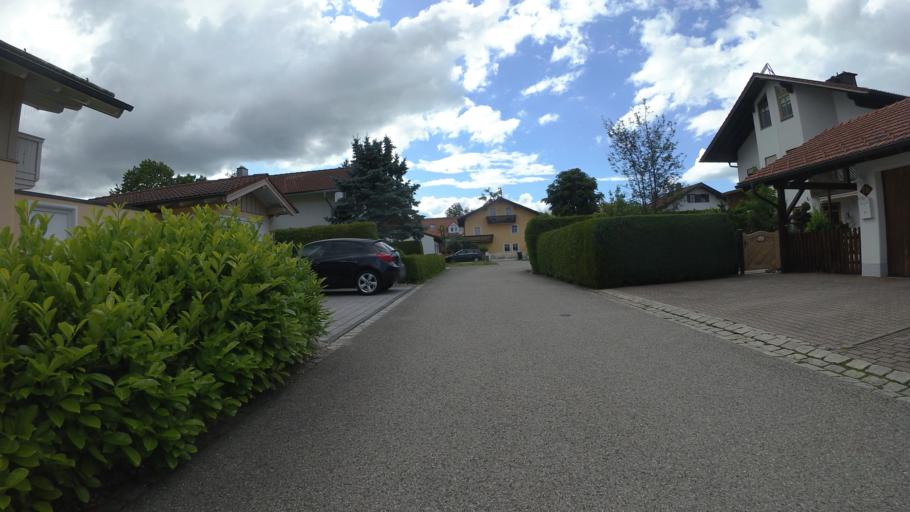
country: DE
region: Bavaria
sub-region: Upper Bavaria
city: Grabenstatt
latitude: 47.8323
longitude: 12.5301
